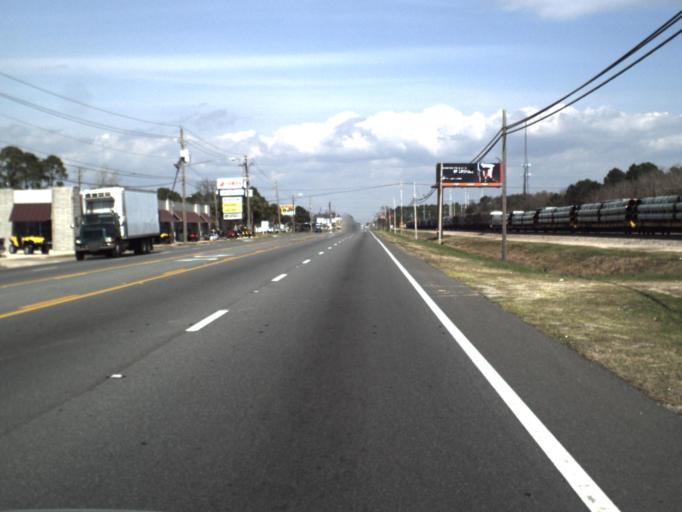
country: US
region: Florida
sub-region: Bay County
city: Hiland Park
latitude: 30.1908
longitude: -85.6389
